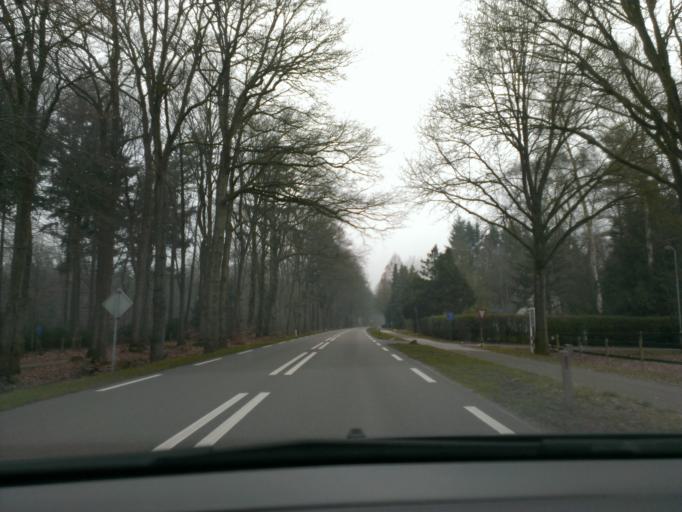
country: NL
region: Gelderland
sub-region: Gemeente Heerde
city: Heerde
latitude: 52.3987
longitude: 6.0298
